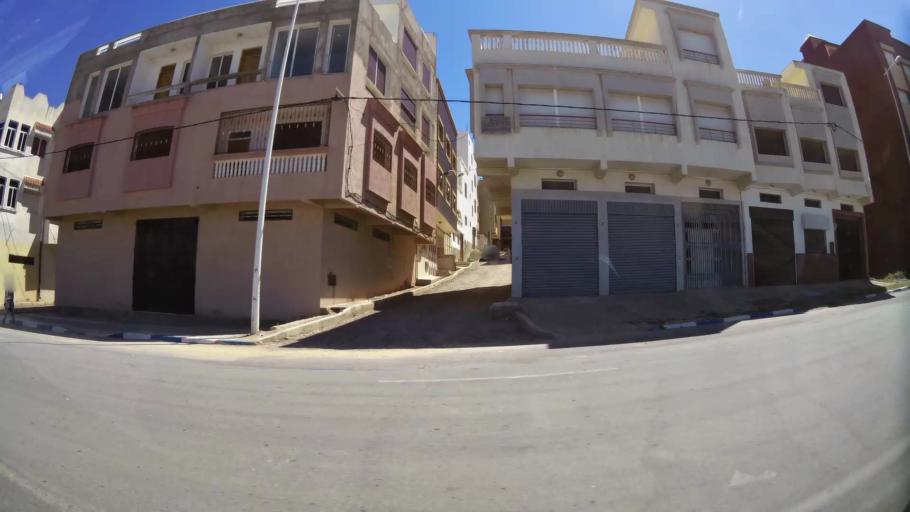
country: MA
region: Oriental
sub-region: Berkane-Taourirt
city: Madagh
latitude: 35.1373
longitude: -2.4178
